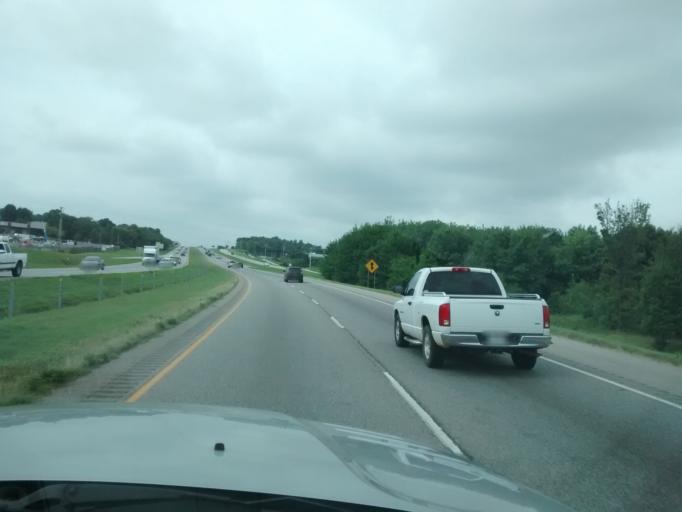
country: US
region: Arkansas
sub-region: Washington County
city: Johnson
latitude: 36.1052
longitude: -94.1806
